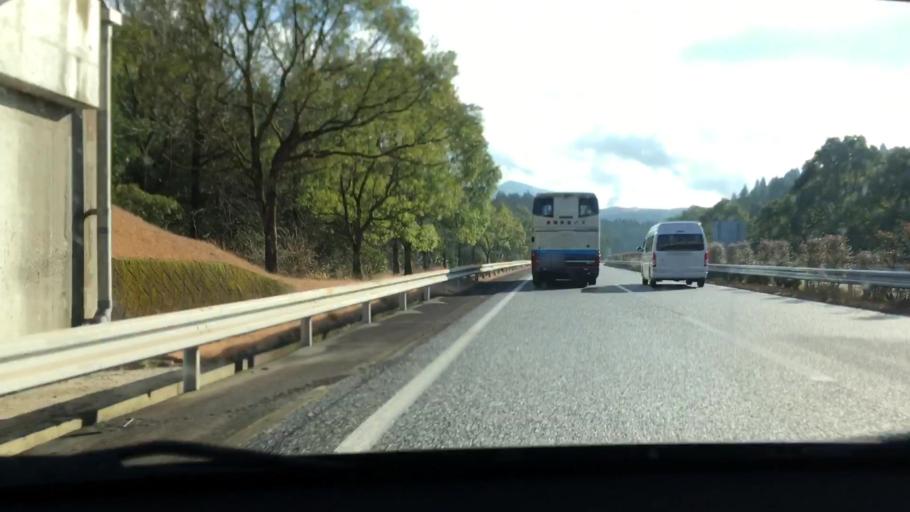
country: JP
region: Kagoshima
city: Okuchi-shinohara
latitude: 32.0330
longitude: 130.7982
